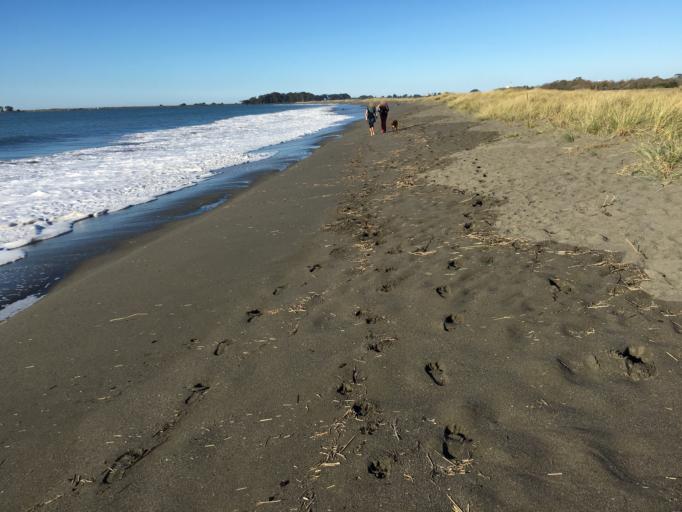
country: US
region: California
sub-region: Humboldt County
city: Bayview
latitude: 40.7566
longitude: -124.1973
